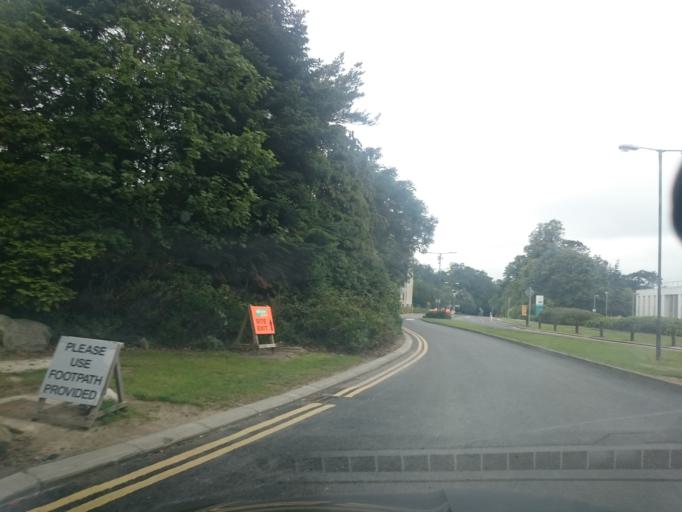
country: IE
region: Leinster
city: Foxrock
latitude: 53.2690
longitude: -6.1989
